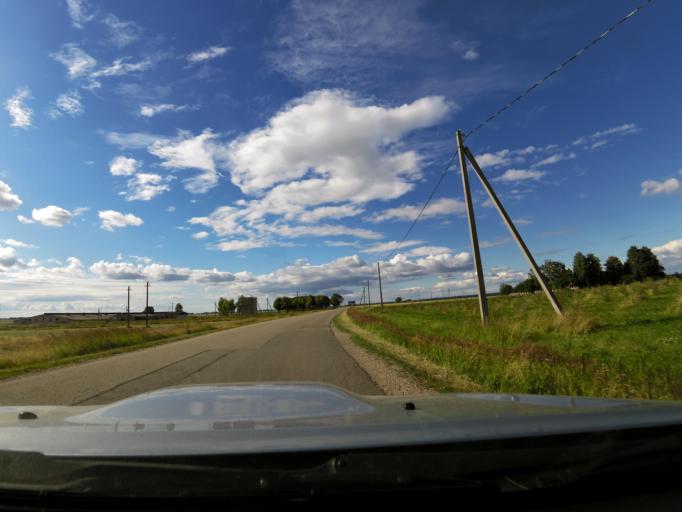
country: LT
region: Panevezys
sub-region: Birzai
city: Birzai
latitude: 56.2799
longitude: 24.8189
